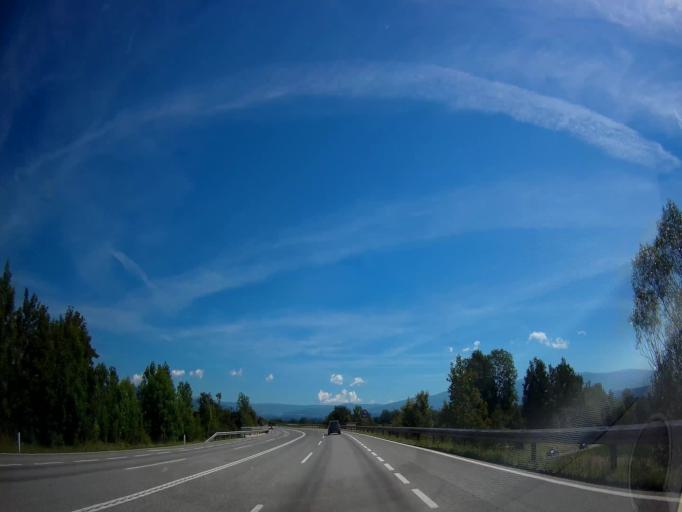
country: AT
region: Carinthia
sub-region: Politischer Bezirk Sankt Veit an der Glan
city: Molbling
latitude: 46.8208
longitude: 14.4362
